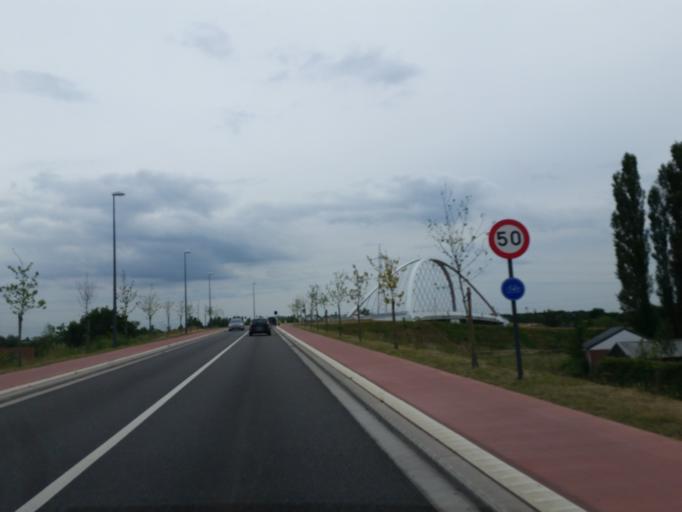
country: BE
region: Flanders
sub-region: Provincie Antwerpen
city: Schilde
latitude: 51.2091
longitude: 4.6004
